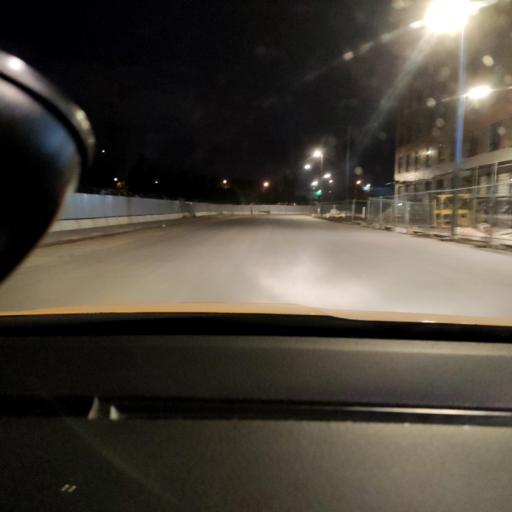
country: RU
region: Moscow
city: Mar'ino
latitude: 55.6613
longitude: 37.7343
